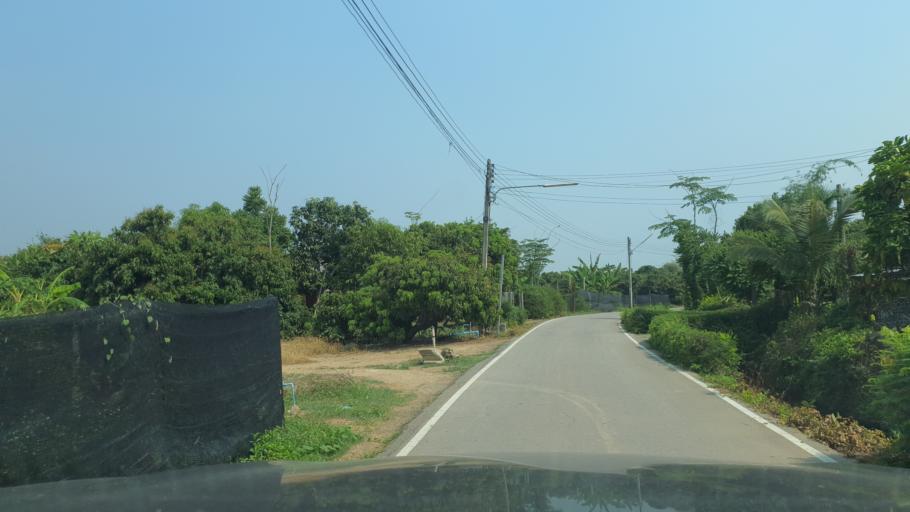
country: TH
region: Lamphun
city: Lamphun
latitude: 18.6515
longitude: 98.9881
